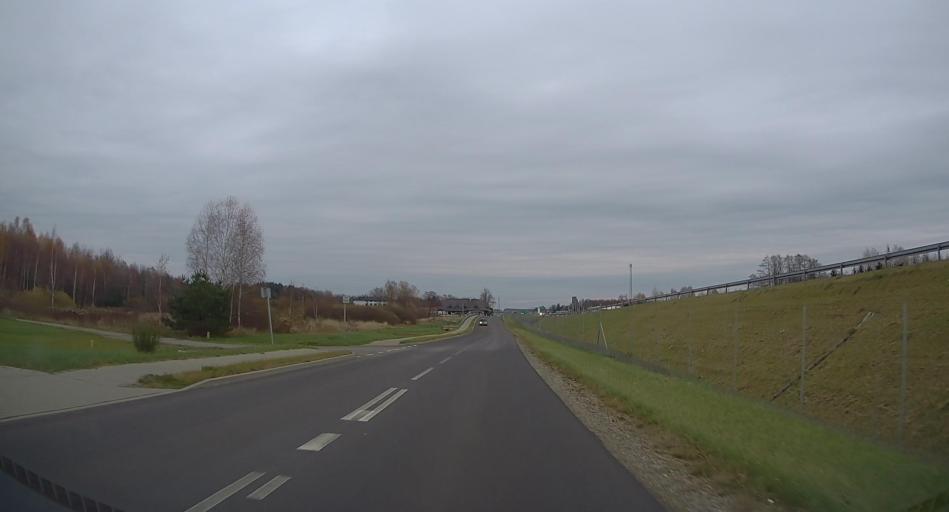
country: PL
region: Lodz Voivodeship
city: Zabia Wola
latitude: 52.0218
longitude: 20.6390
